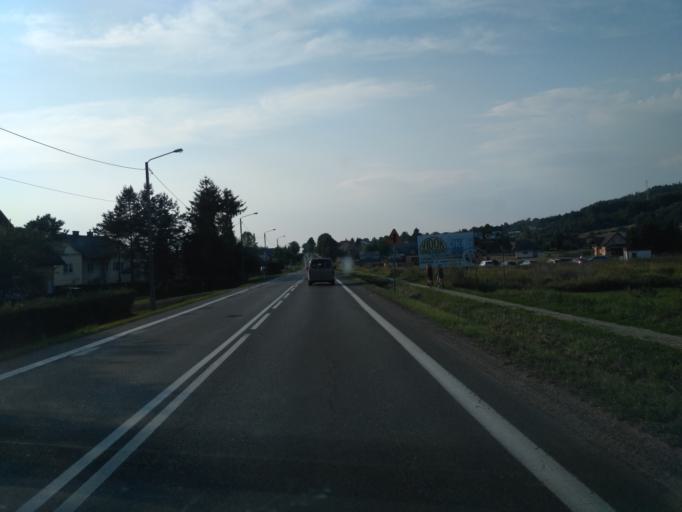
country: PL
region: Subcarpathian Voivodeship
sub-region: Powiat brzozowski
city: Stara Wies
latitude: 49.7354
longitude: 21.9957
